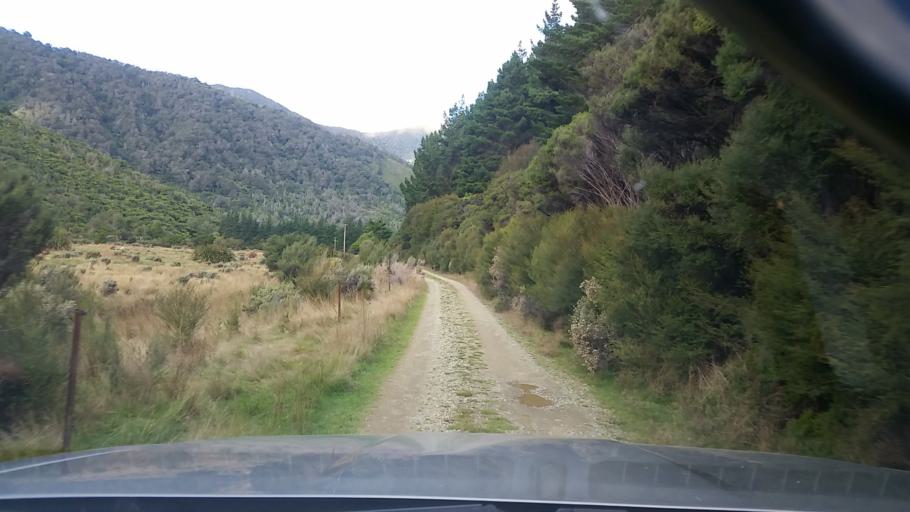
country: NZ
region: Marlborough
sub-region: Marlborough District
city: Picton
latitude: -41.0624
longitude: 174.1182
